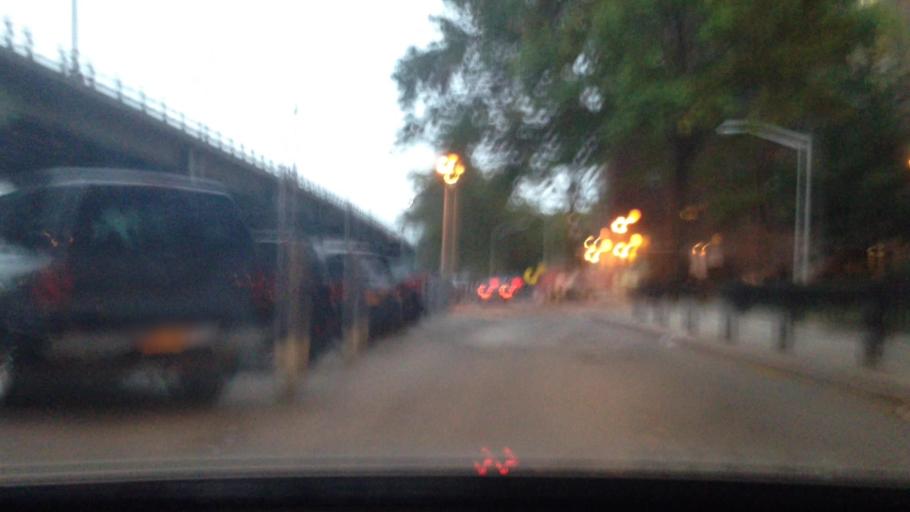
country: US
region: New York
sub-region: New York County
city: Inwood
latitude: 40.8328
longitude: -73.9356
